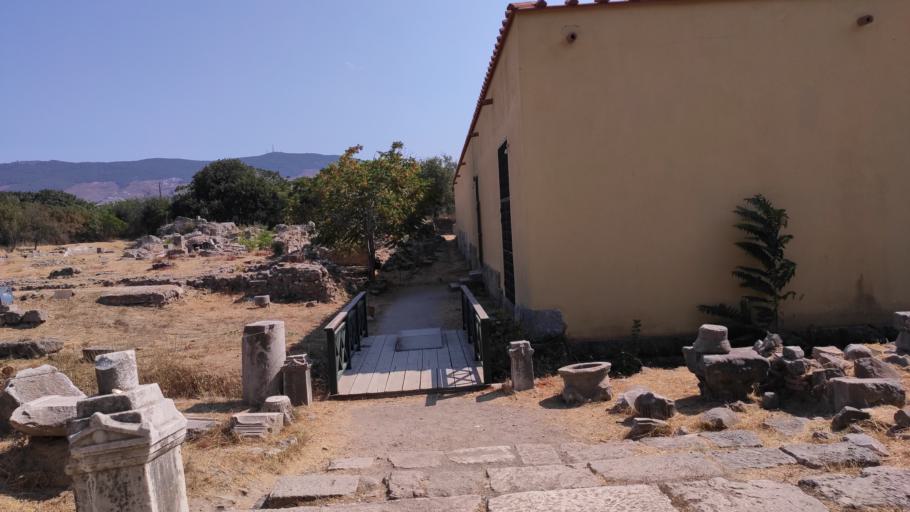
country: GR
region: South Aegean
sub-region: Nomos Dodekanisou
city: Kos
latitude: 36.8903
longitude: 27.2886
